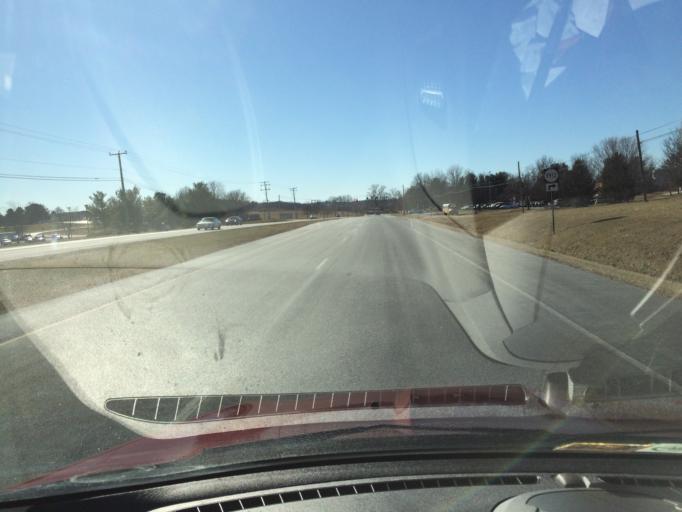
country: US
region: Virginia
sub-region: Rockingham County
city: Dayton
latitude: 38.3983
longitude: -78.9573
